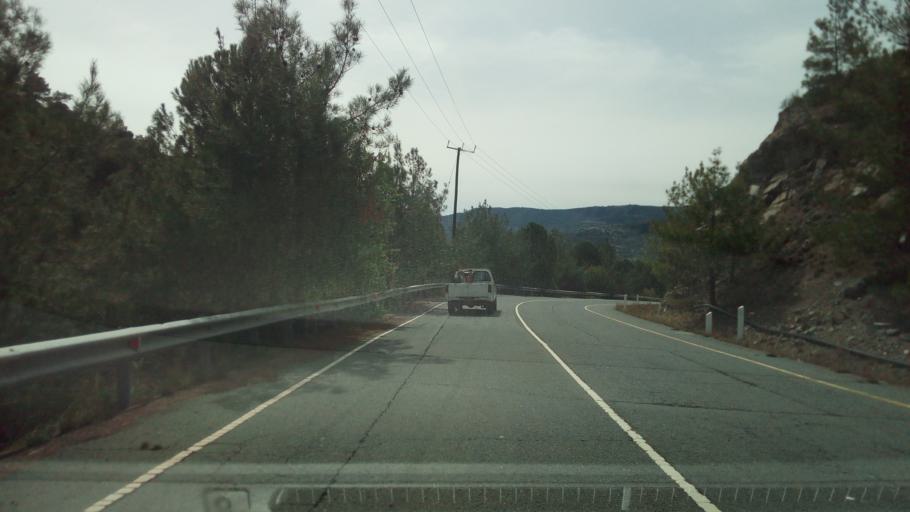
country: CY
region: Limassol
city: Pelendri
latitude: 34.8655
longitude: 32.9220
